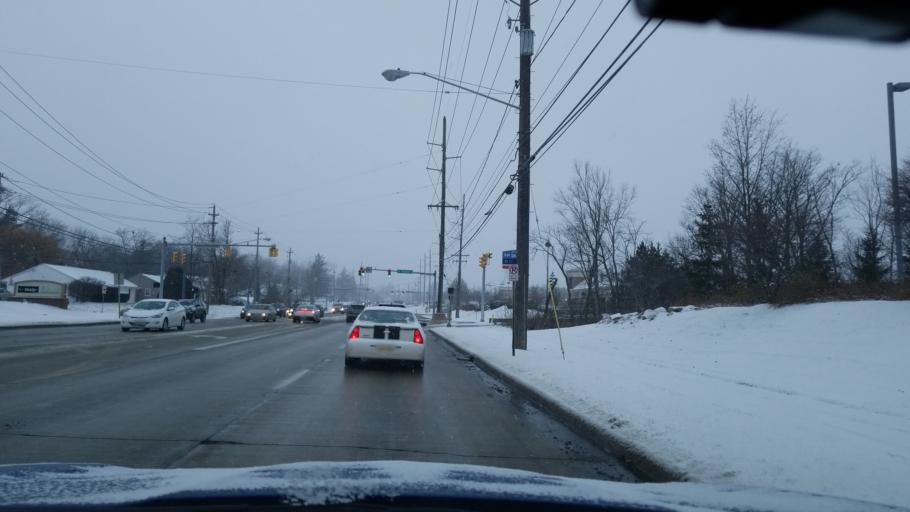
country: US
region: Ohio
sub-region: Cuyahoga County
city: Strongsville
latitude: 41.3134
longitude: -81.8267
